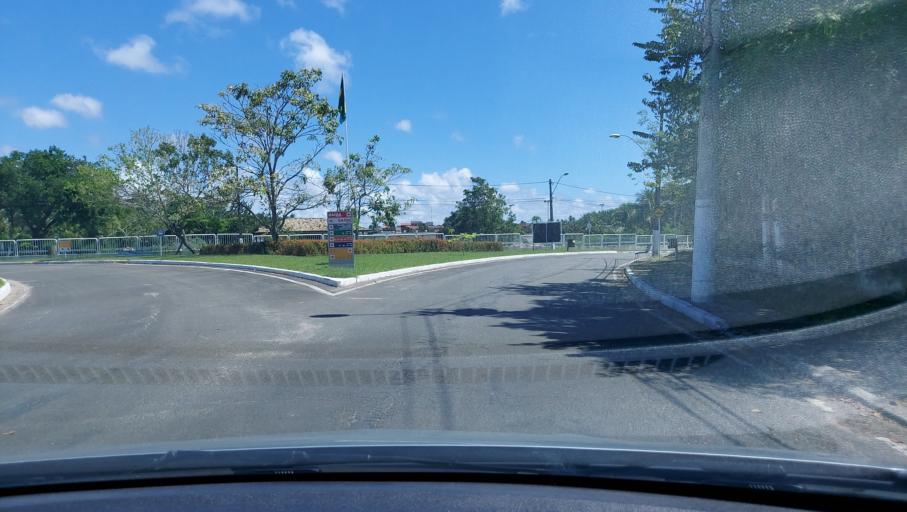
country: BR
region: Bahia
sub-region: Lauro De Freitas
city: Lauro de Freitas
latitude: -12.8687
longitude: -38.3095
